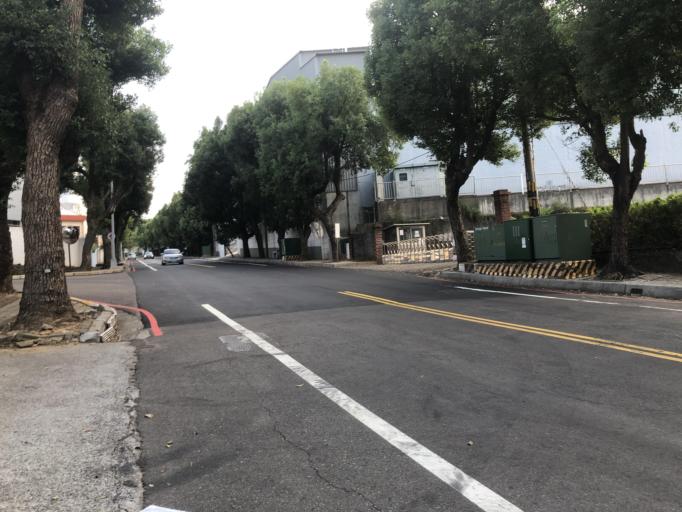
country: TW
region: Taiwan
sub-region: Miaoli
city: Miaoli
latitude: 24.4805
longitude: 120.7925
